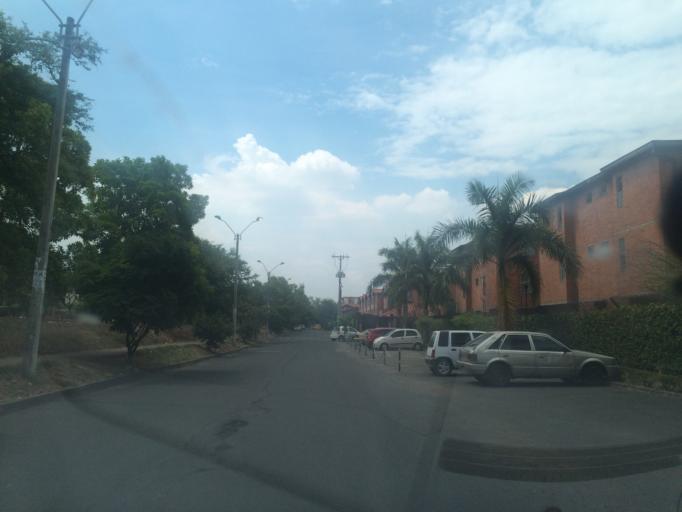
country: CO
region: Valle del Cauca
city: Cali
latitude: 3.3732
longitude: -76.5220
